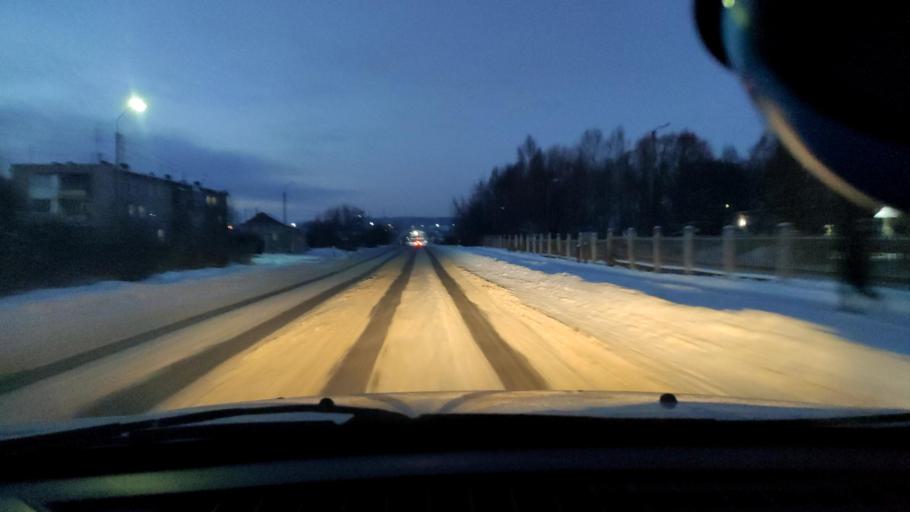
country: RU
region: Perm
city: Kultayevo
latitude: 57.8963
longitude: 55.9310
